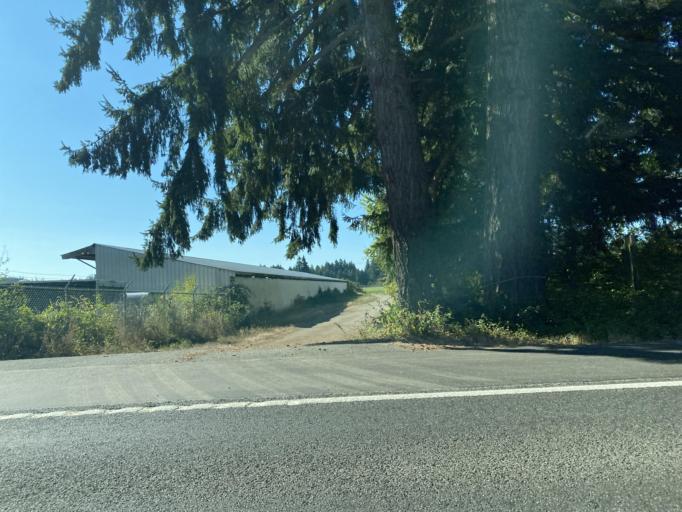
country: US
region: Washington
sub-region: Thurston County
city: Tanglewilde-Thompson Place
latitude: 46.9845
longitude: -122.7615
